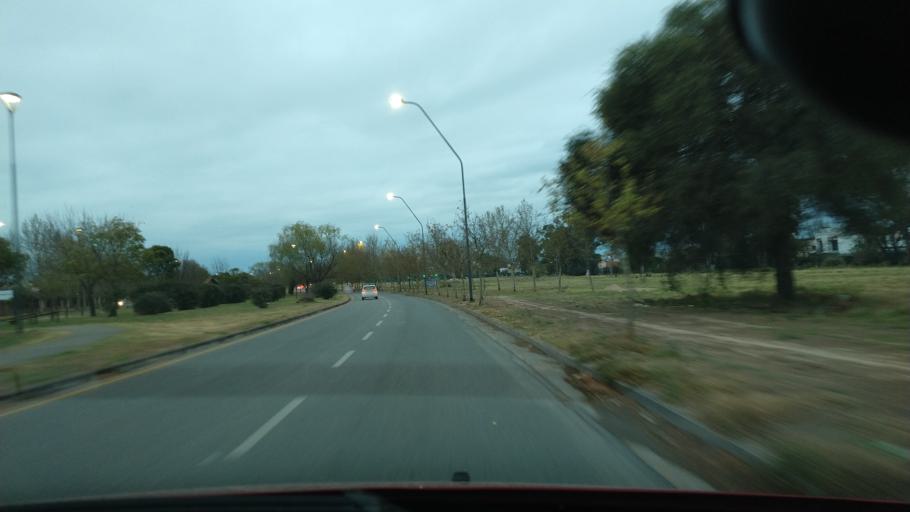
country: AR
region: Cordoba
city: La Calera
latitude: -31.3771
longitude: -64.2767
